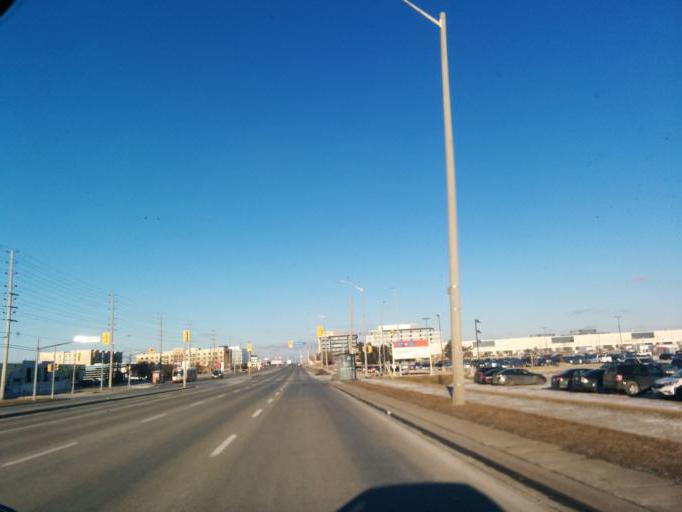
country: CA
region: Ontario
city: Etobicoke
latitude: 43.6377
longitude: -79.6183
